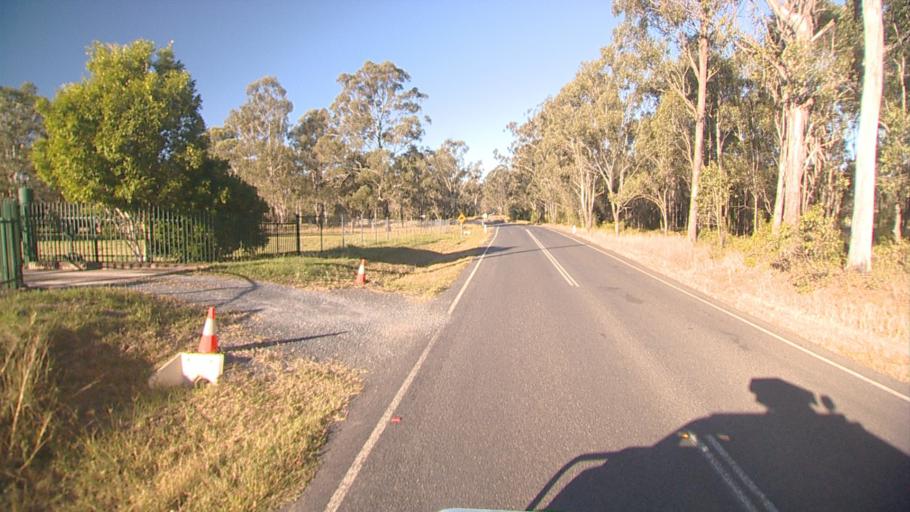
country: AU
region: Queensland
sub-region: Logan
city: North Maclean
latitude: -27.7596
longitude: 153.0435
